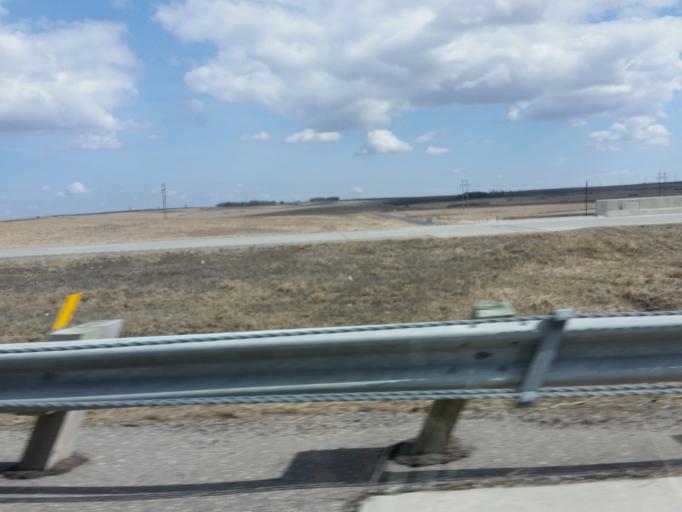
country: US
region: South Dakota
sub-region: Codington County
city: Watertown
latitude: 45.2244
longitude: -97.0513
